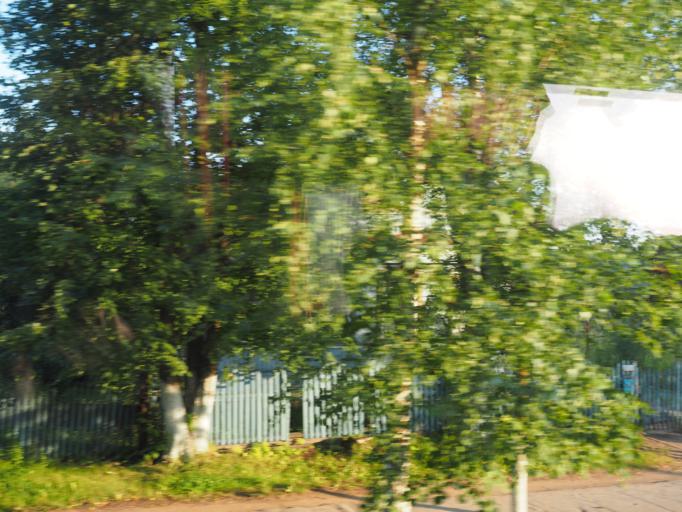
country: RU
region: Vologda
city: Chagoda
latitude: 59.1625
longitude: 35.3218
